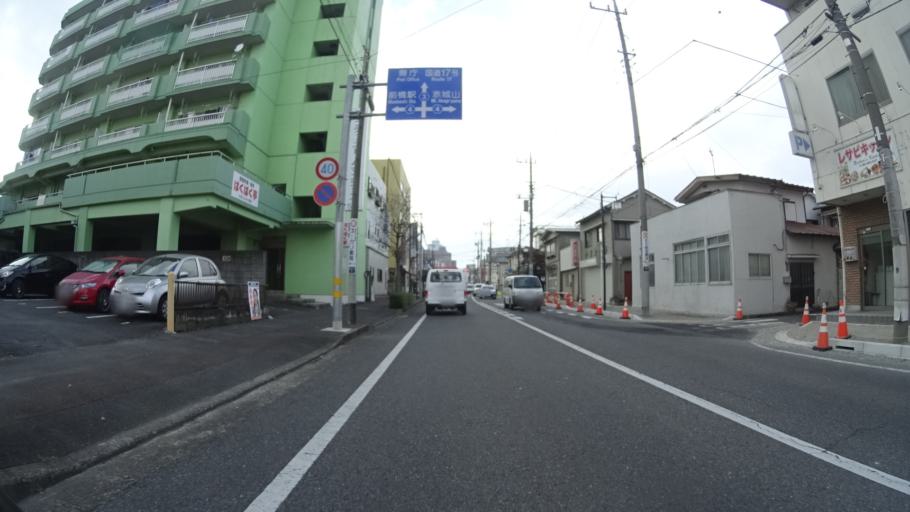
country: JP
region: Gunma
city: Maebashi-shi
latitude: 36.3934
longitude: 139.0757
